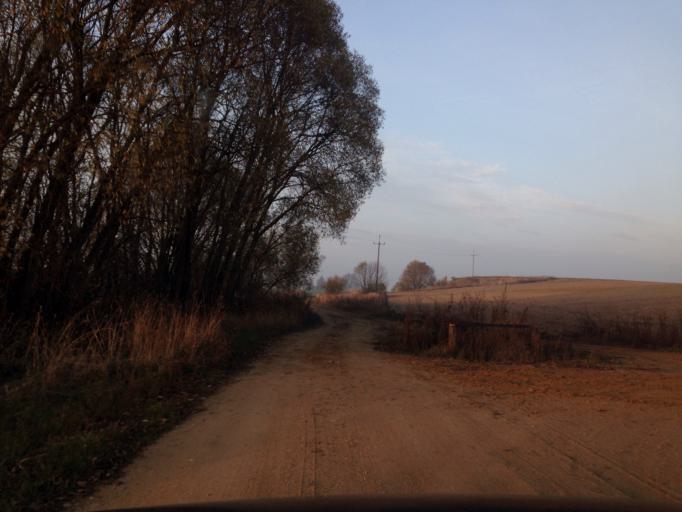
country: PL
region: Warmian-Masurian Voivodeship
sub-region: Powiat dzialdowski
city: Lidzbark
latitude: 53.2607
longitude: 19.7735
